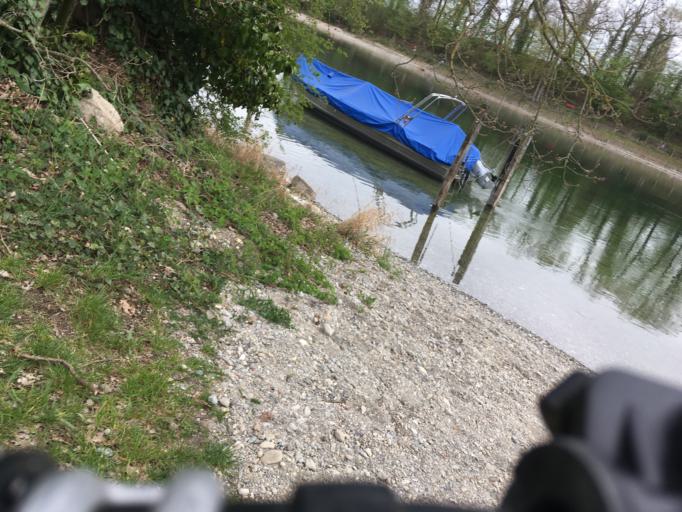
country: CH
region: Thurgau
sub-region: Frauenfeld District
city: Diessenhofen
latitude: 47.6924
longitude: 8.7208
